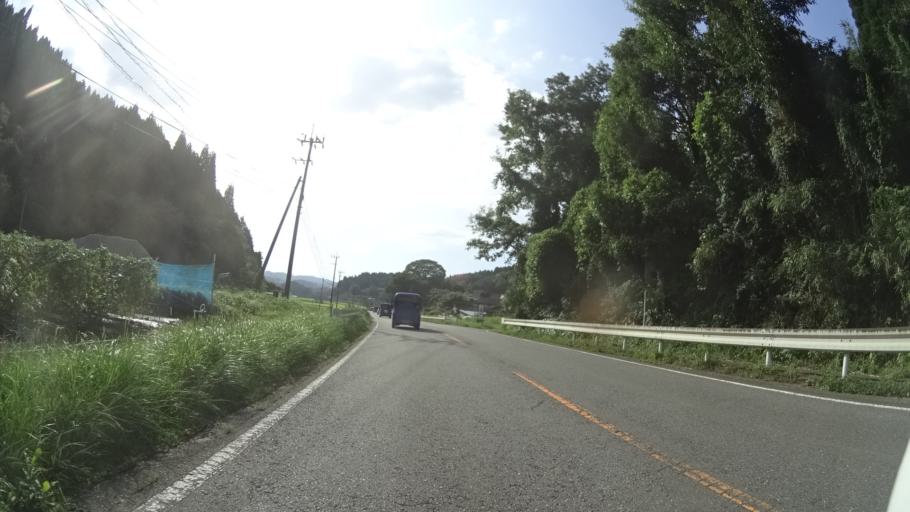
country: JP
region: Kumamoto
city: Ozu
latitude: 32.6797
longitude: 131.0225
